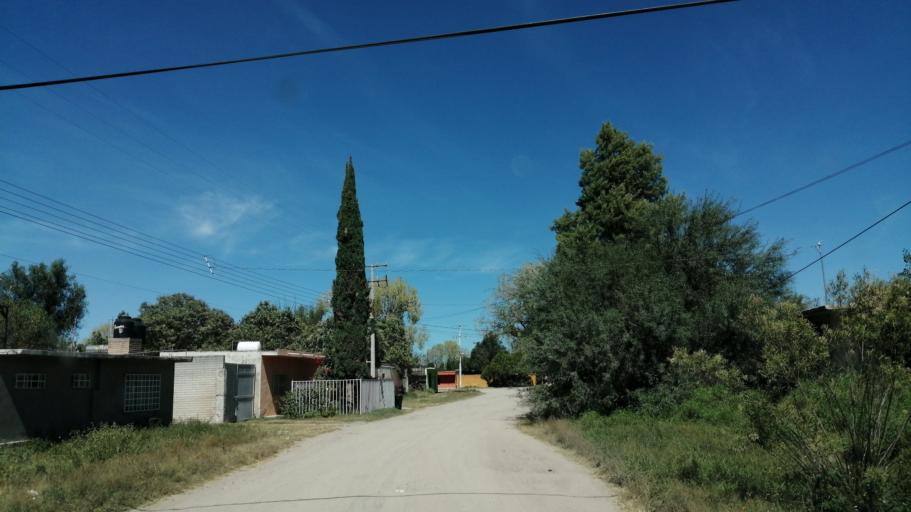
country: MX
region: Durango
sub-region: Santiago Papasquiaro
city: Santiago Papasquiaro
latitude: 25.0336
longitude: -105.4102
